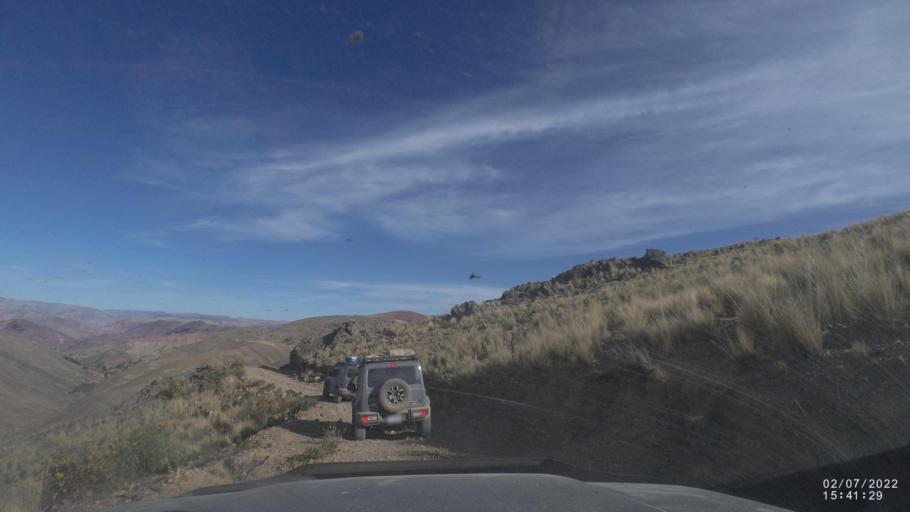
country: BO
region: Cochabamba
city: Irpa Irpa
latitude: -17.9008
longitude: -66.4104
